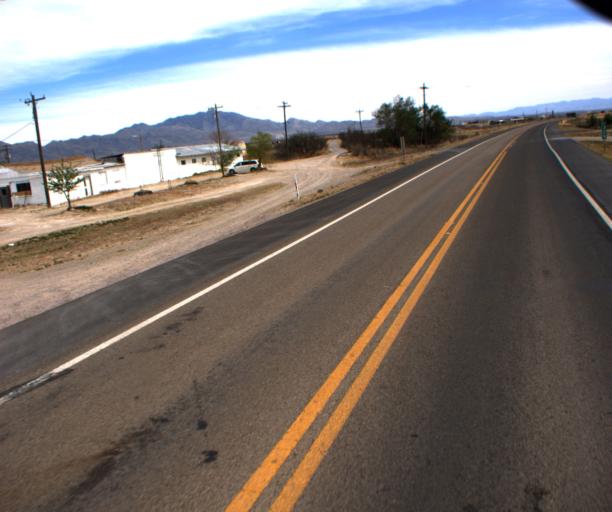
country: US
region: Arizona
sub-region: Cochise County
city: Willcox
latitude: 32.2469
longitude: -109.8213
